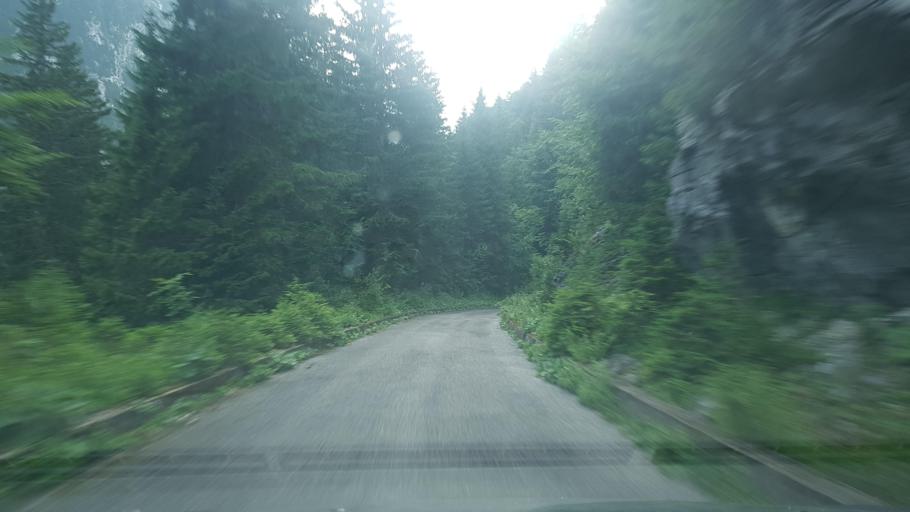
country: IT
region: Friuli Venezia Giulia
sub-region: Provincia di Udine
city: Paularo
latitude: 46.5753
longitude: 13.1457
